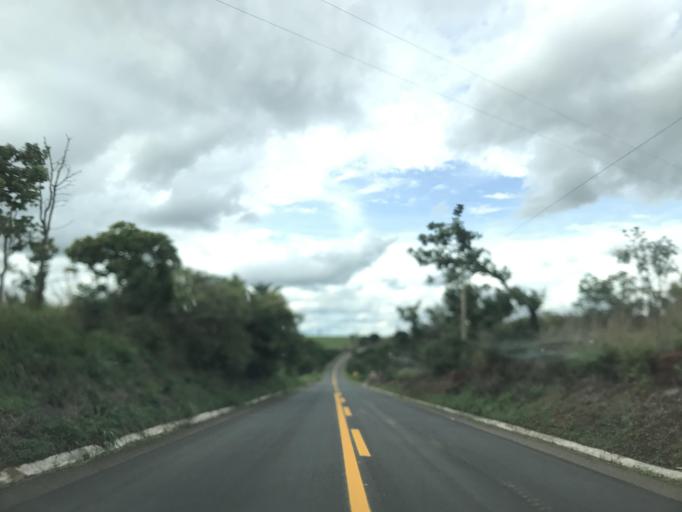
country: BR
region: Goias
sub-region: Bela Vista De Goias
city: Bela Vista de Goias
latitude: -17.0824
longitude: -48.6554
